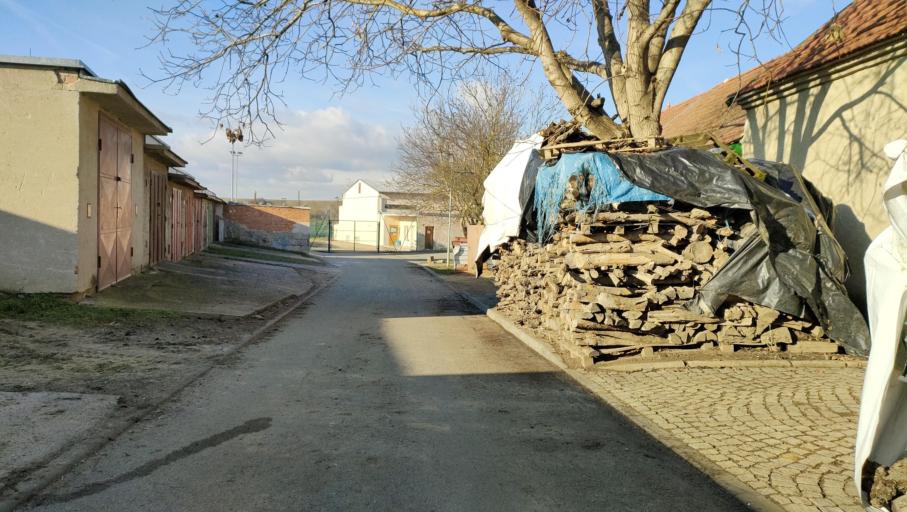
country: CZ
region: South Moravian
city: Sokolnice
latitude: 49.1368
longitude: 16.7321
